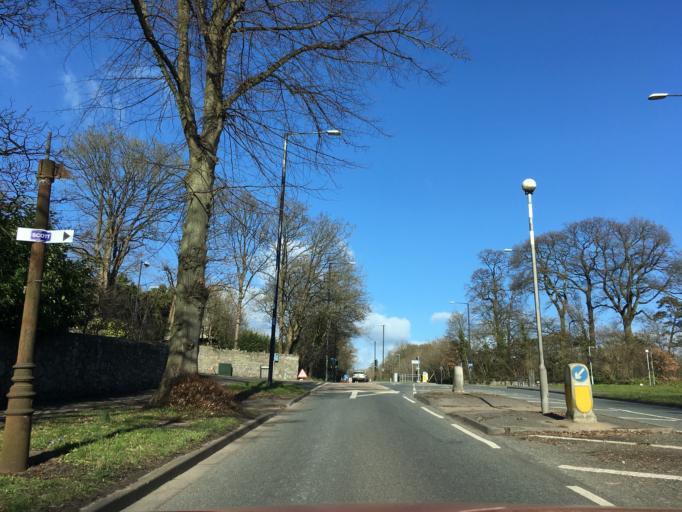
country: GB
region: England
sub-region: Bristol
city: Bristol
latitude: 51.5018
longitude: -2.6161
